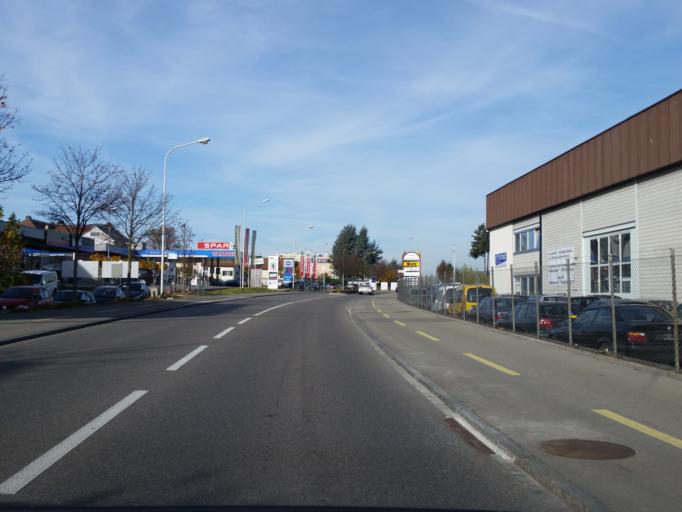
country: CH
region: Thurgau
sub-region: Kreuzlingen District
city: Kreuzlingen
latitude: 47.6441
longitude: 9.1878
